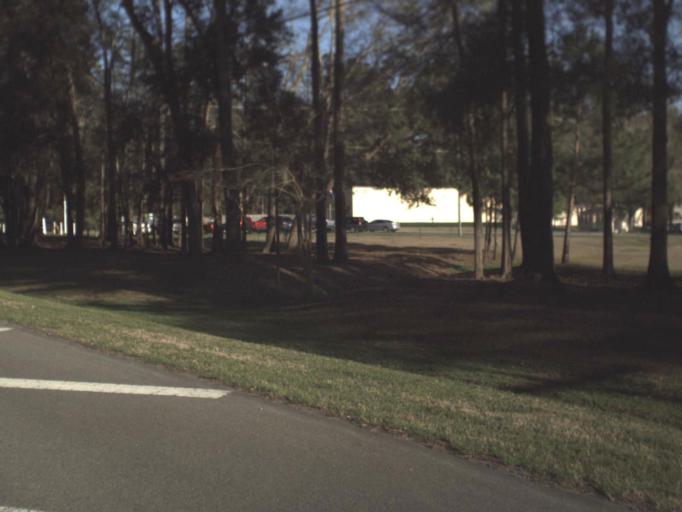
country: US
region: Florida
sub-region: Leon County
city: Tallahassee
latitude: 30.4882
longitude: -84.1480
